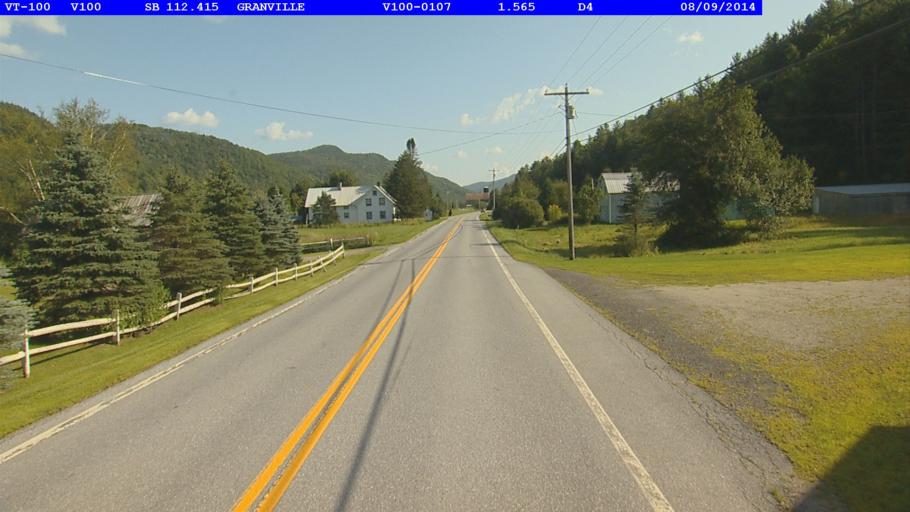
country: US
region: Vermont
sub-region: Orange County
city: Randolph
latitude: 43.9669
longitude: -72.8426
